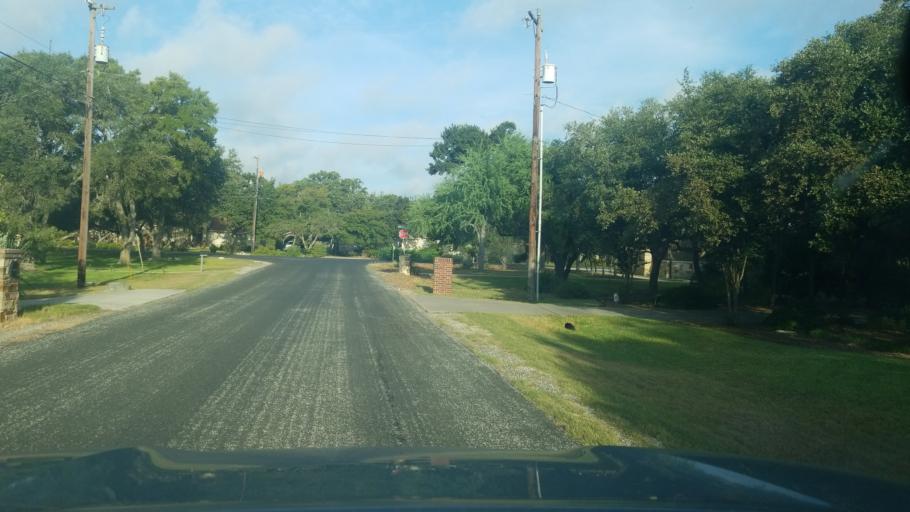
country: US
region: Texas
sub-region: Bexar County
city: Timberwood Park
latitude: 29.6992
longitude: -98.5059
